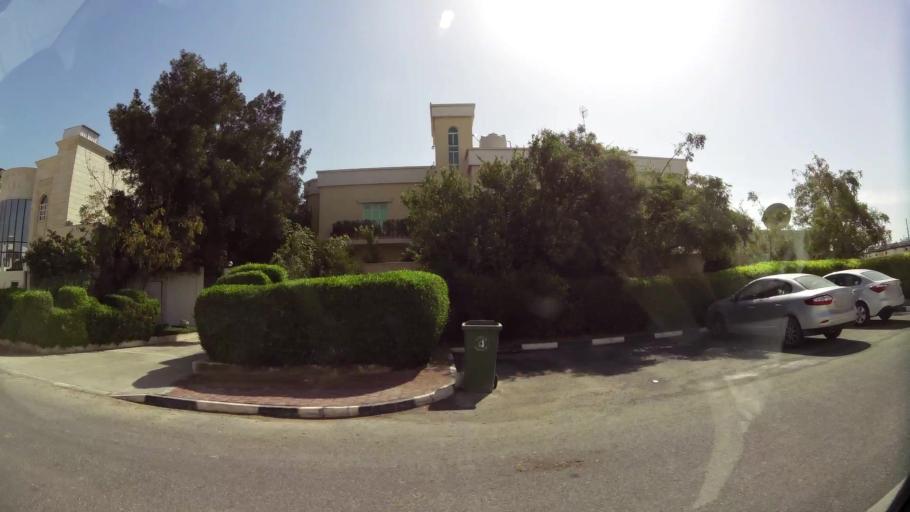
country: QA
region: Baladiyat ad Dawhah
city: Doha
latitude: 25.3532
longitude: 51.5191
